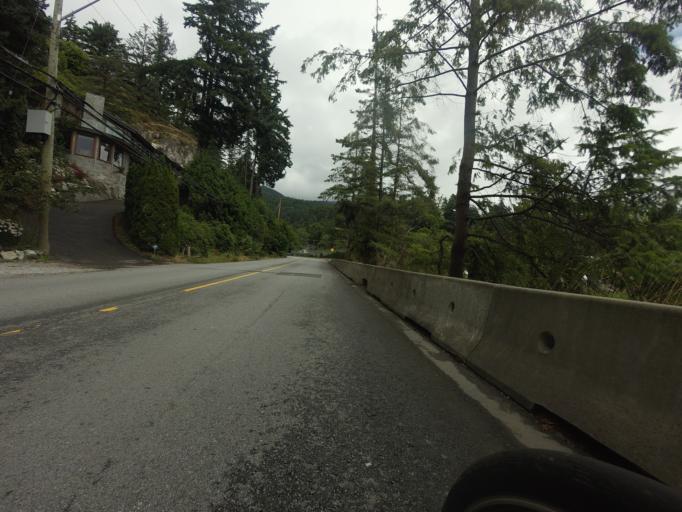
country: CA
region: British Columbia
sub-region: Greater Vancouver Regional District
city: Bowen Island
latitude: 49.3582
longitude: -123.2696
